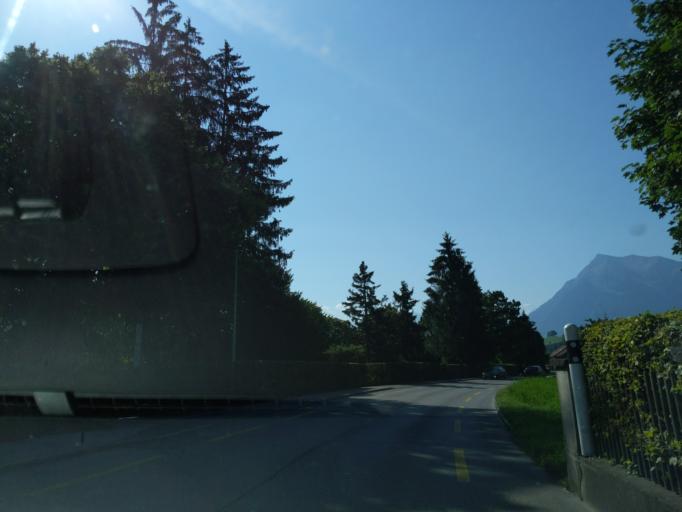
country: CH
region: Bern
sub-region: Thun District
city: Thun
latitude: 46.7320
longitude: 7.6126
